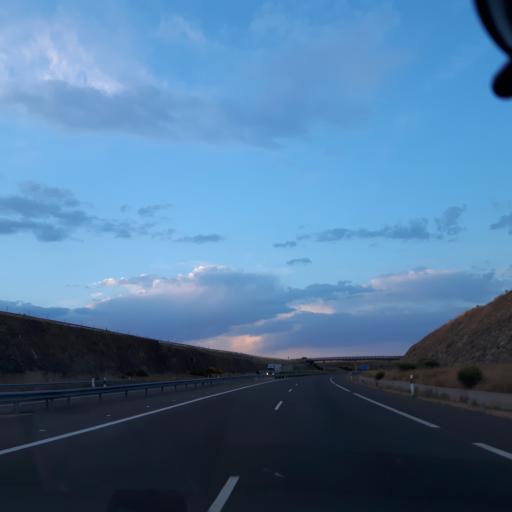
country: ES
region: Castille and Leon
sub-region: Provincia de Salamanca
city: Mozarbez
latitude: 40.8633
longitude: -5.6452
